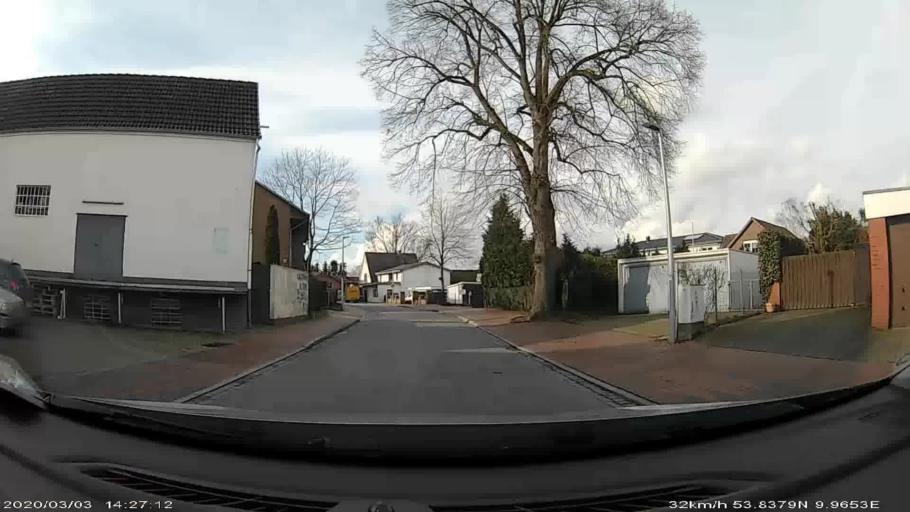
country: DE
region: Schleswig-Holstein
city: Kaltenkirchen
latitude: 53.8381
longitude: 9.9653
